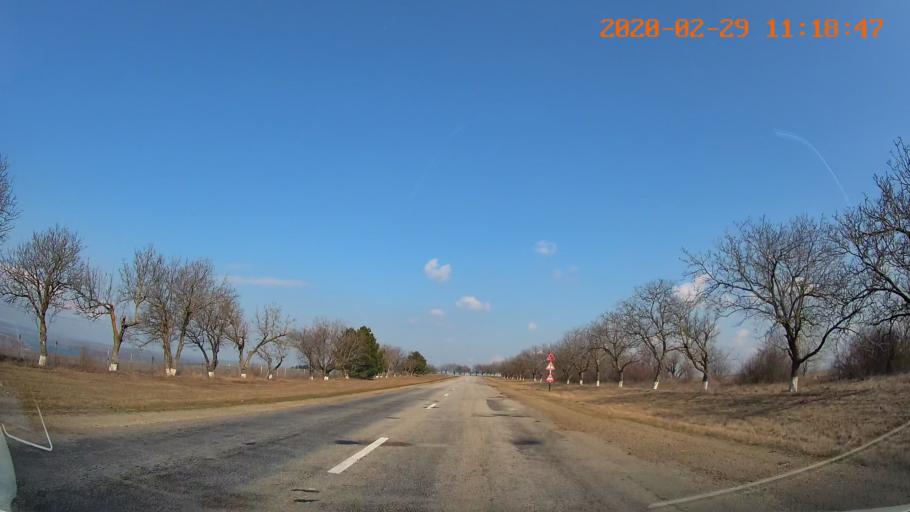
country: MD
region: Telenesti
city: Cocieri
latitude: 47.3401
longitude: 29.1752
